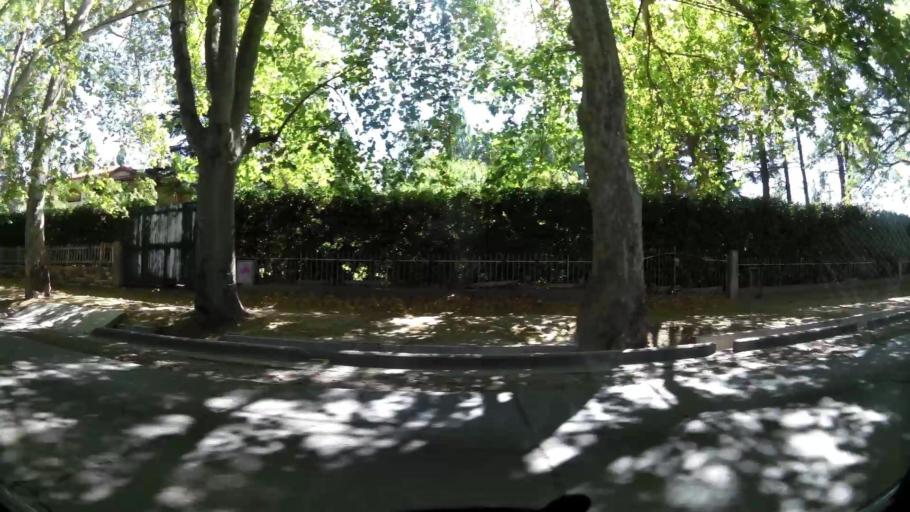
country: AR
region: Mendoza
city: Lujan de Cuyo
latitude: -32.9857
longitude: -68.8614
